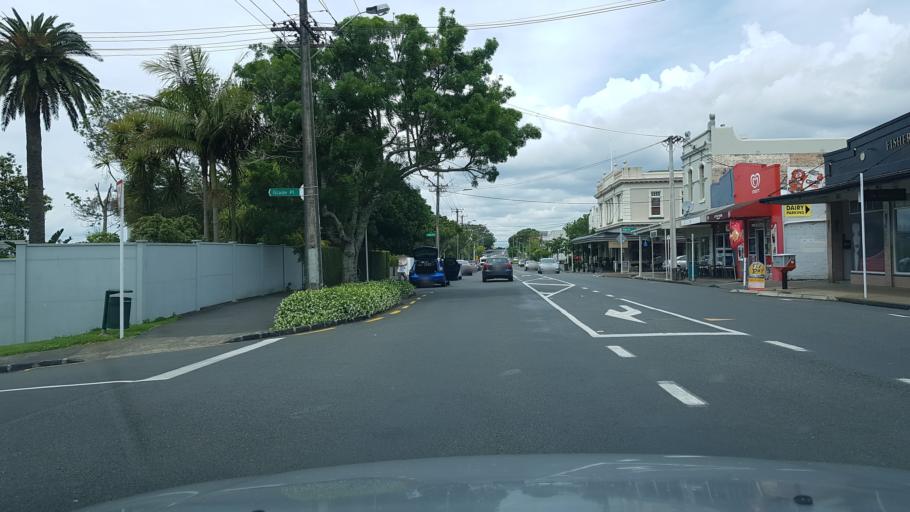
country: NZ
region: Auckland
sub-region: Auckland
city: North Shore
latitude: -36.8163
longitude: 174.7320
